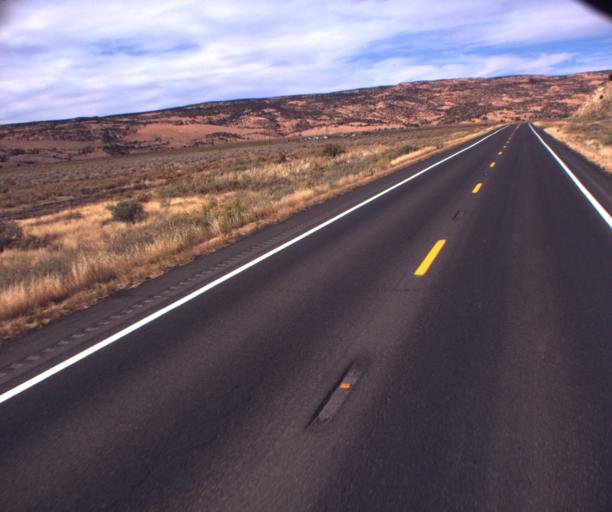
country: US
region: Arizona
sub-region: Navajo County
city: Kayenta
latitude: 36.6047
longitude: -110.4728
